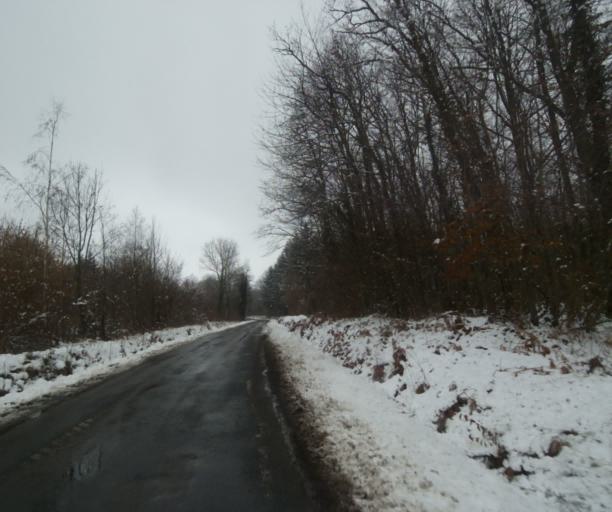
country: FR
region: Champagne-Ardenne
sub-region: Departement de la Haute-Marne
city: Laneuville-a-Remy
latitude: 48.4668
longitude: 4.8676
